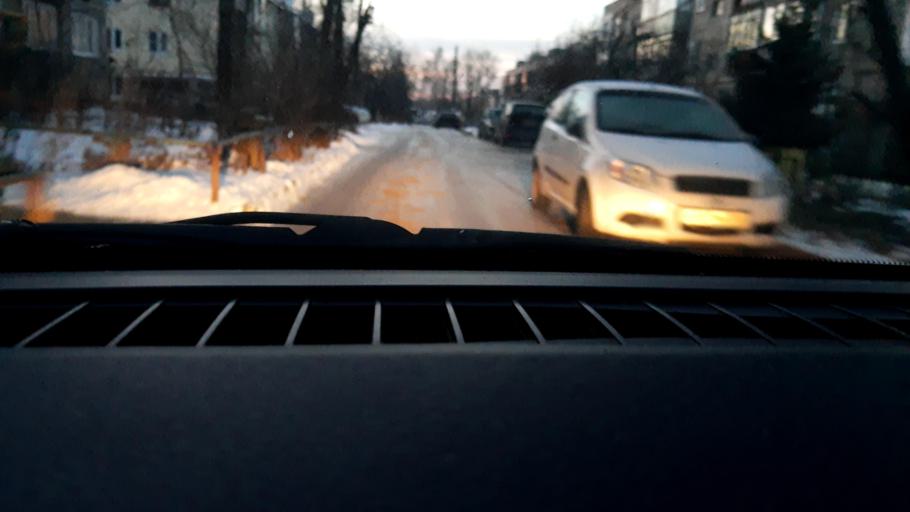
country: RU
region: Nizjnij Novgorod
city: Afonino
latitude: 56.2091
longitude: 44.0270
